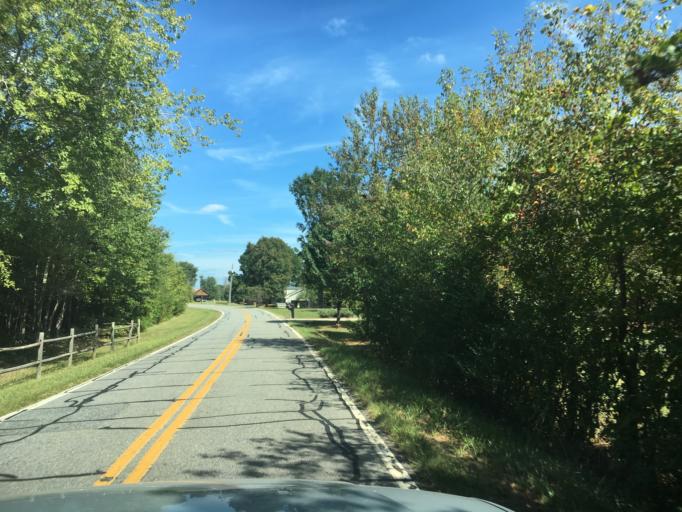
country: US
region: North Carolina
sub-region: Rutherford County
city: Forest City
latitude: 35.2520
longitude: -81.9214
